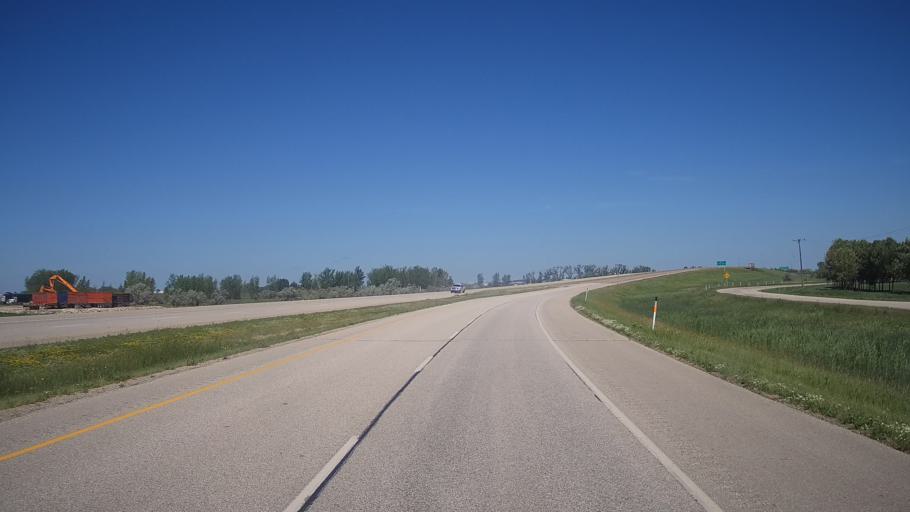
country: CA
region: Manitoba
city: Portage la Prairie
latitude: 49.9629
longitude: -98.3526
